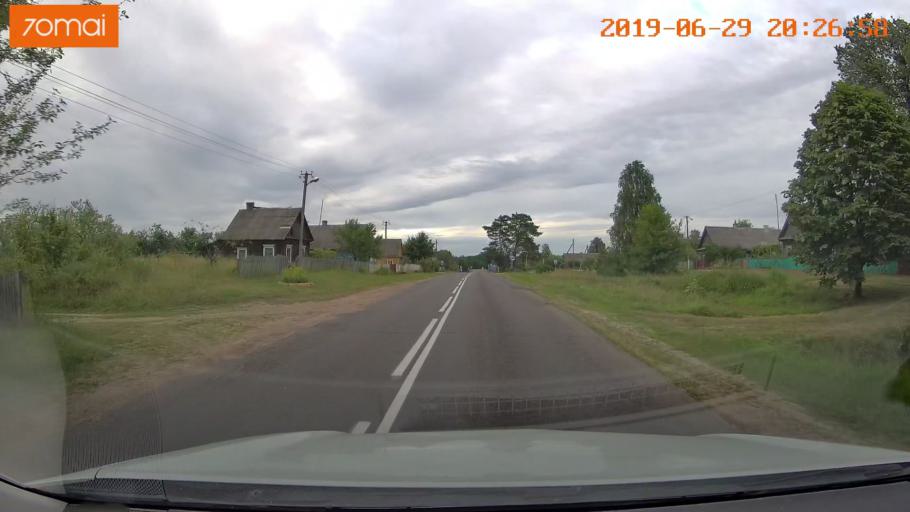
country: BY
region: Brest
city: Hantsavichy
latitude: 52.4707
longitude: 26.3005
